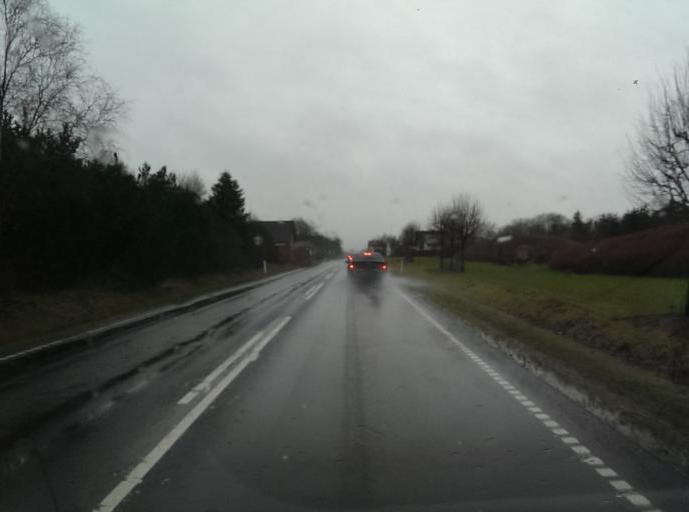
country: DK
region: South Denmark
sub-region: Varde Kommune
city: Olgod
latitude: 55.7138
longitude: 8.6099
